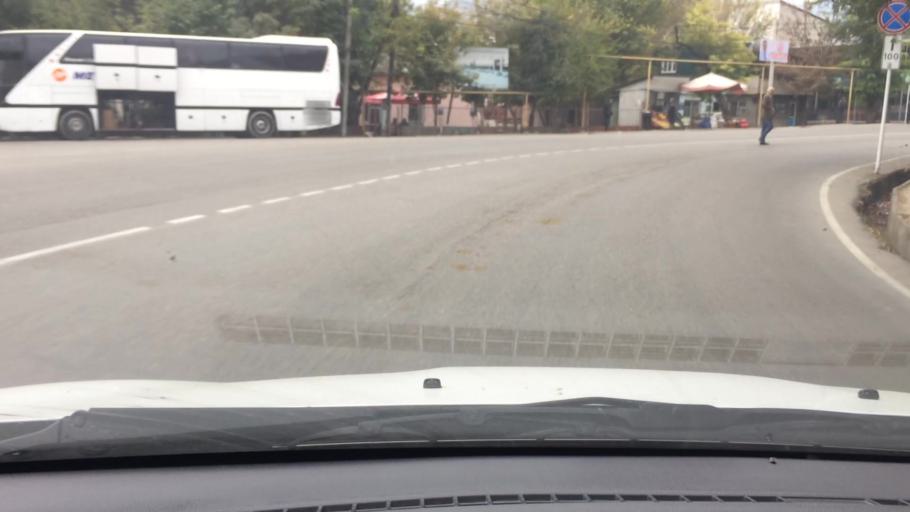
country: AM
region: Tavush
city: Bagratashen
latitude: 41.2463
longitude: 44.7993
